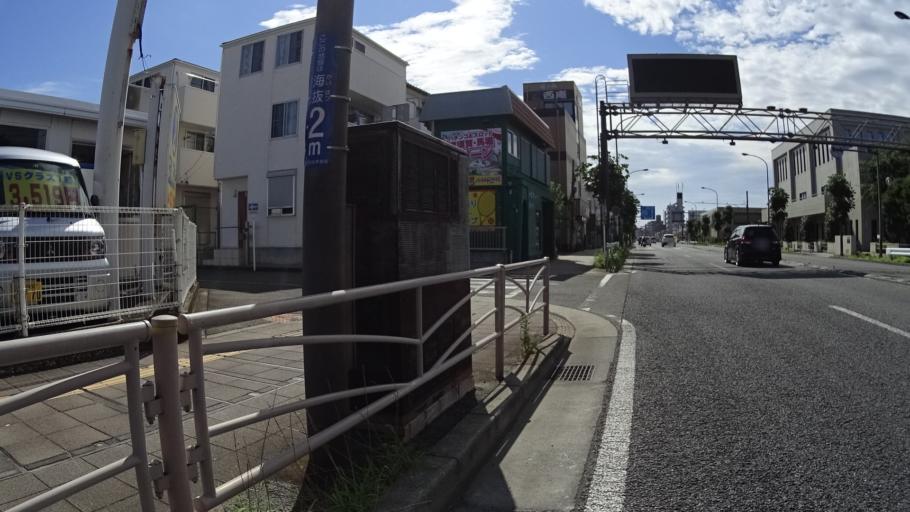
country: JP
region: Kanagawa
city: Yokosuka
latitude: 35.2675
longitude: 139.6852
